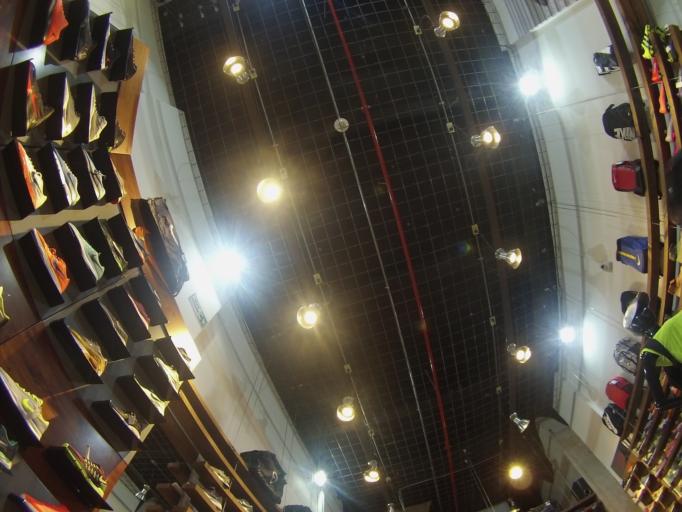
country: CO
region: Quindio
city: Armenia
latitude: 4.5463
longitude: -75.6722
